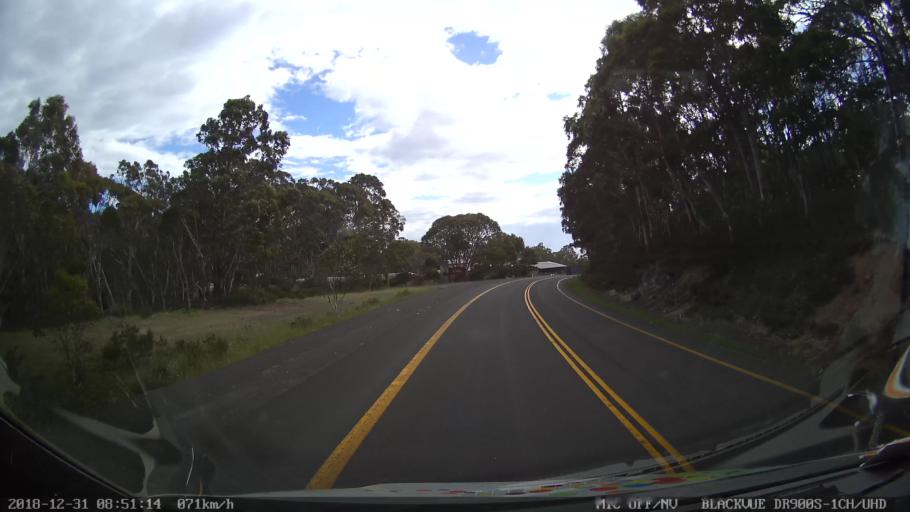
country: AU
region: New South Wales
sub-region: Snowy River
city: Jindabyne
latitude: -36.3476
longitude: 148.5249
